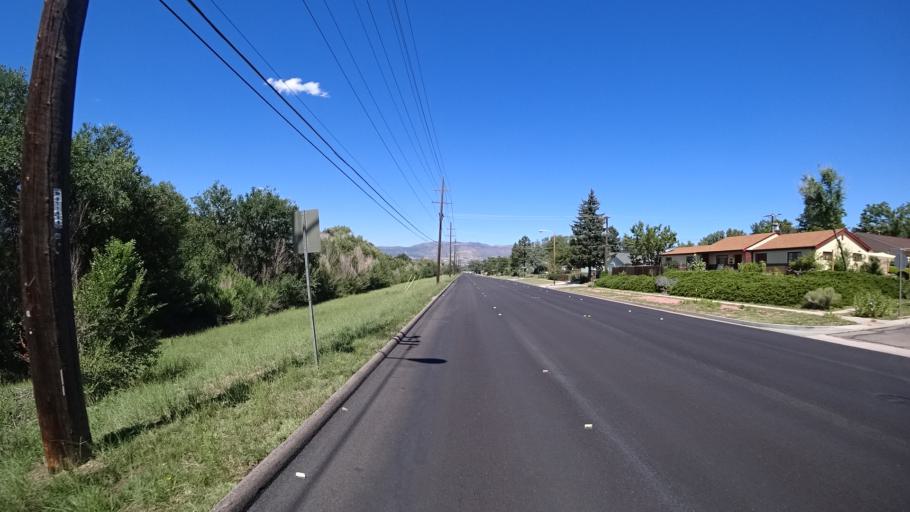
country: US
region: Colorado
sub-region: El Paso County
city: Colorado Springs
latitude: 38.8630
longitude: -104.7968
